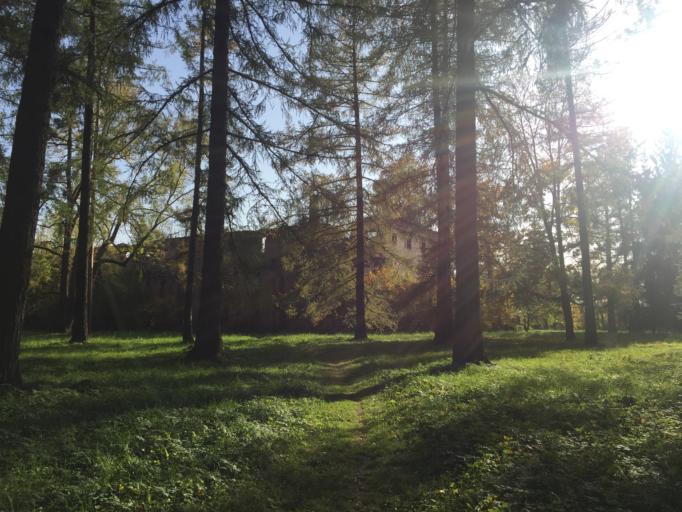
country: RU
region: St.-Petersburg
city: Pushkin
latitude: 59.7186
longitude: 30.3860
